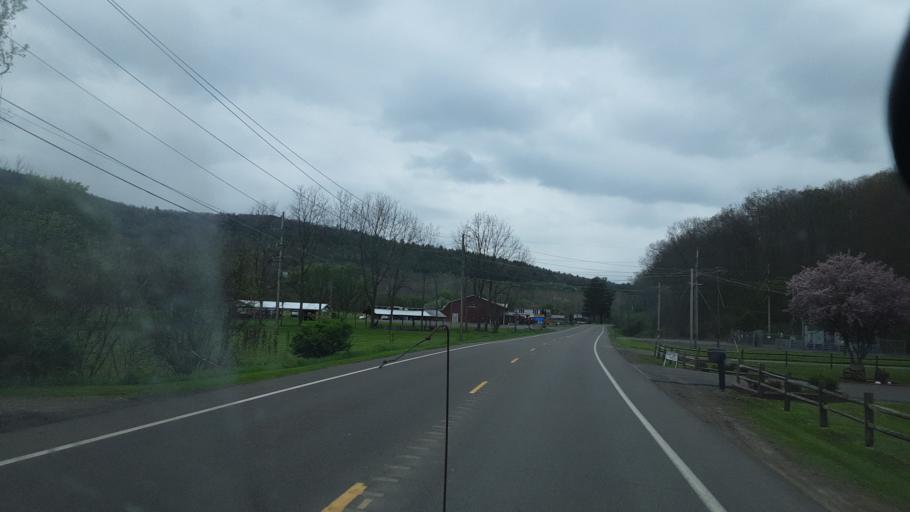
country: US
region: New York
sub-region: Steuben County
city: Addison
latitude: 42.0870
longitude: -77.2471
